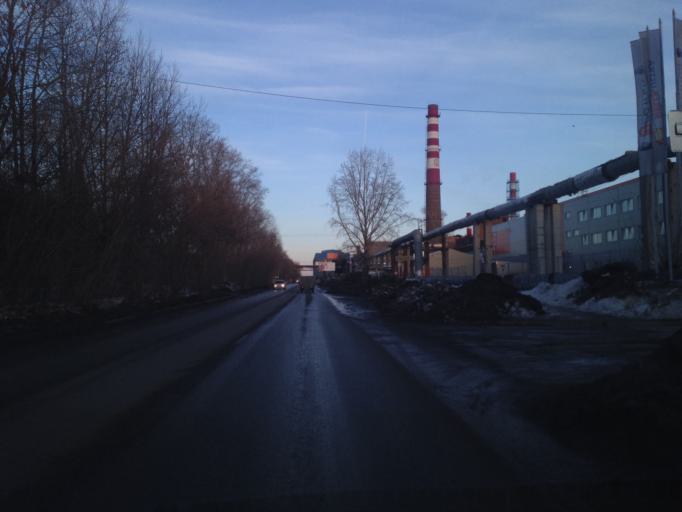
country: RU
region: Sverdlovsk
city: Istok
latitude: 56.7588
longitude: 60.7131
